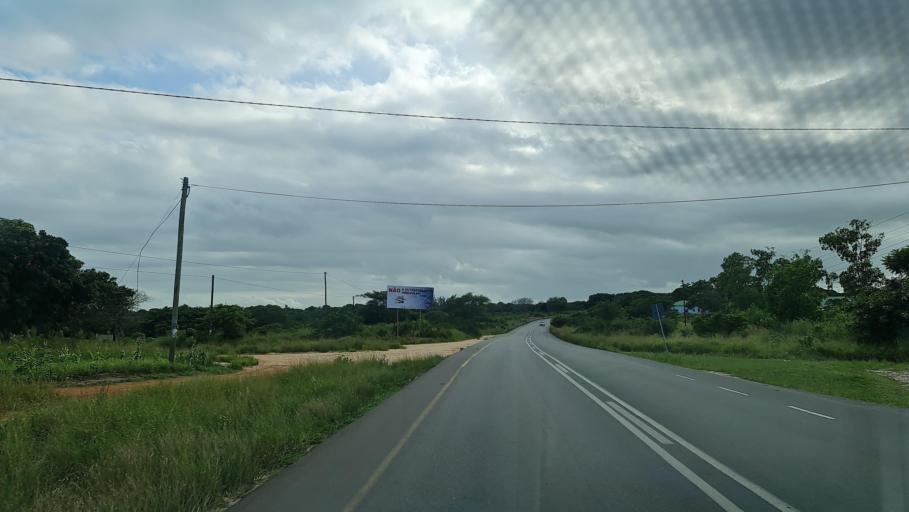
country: MZ
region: Maputo
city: Manhica
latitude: -25.4120
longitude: 32.7424
